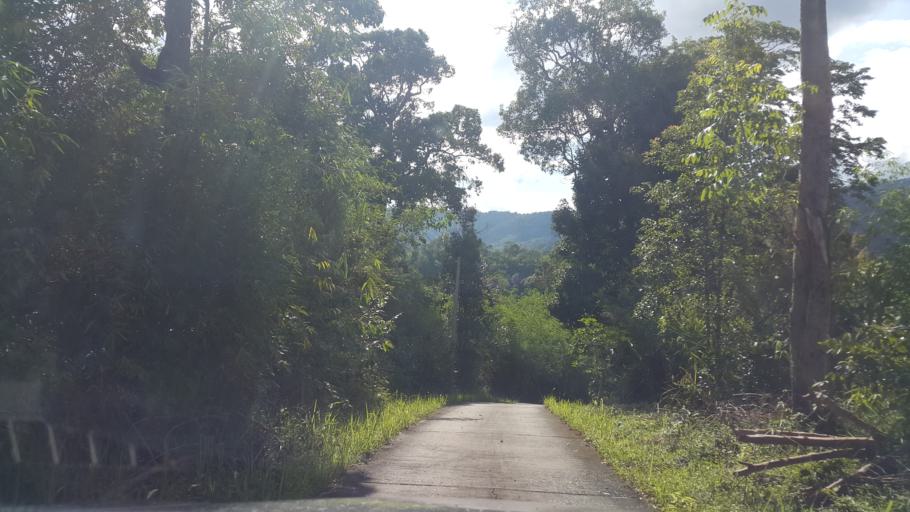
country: TH
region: Loei
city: Na Haeo
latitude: 17.5625
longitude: 100.9512
